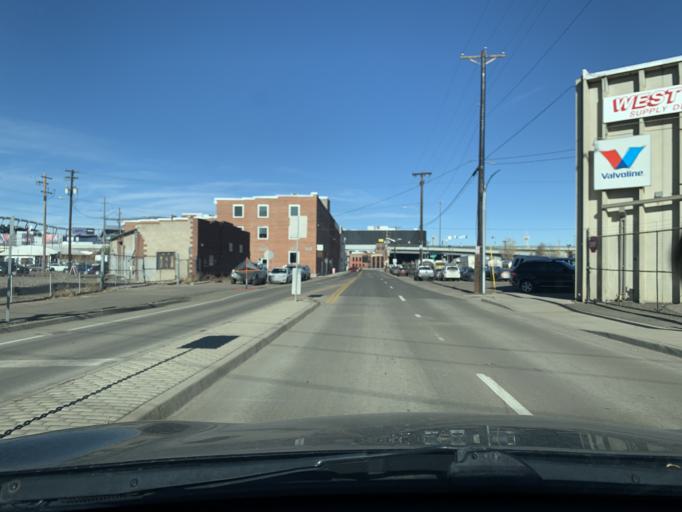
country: US
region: Colorado
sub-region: Denver County
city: Denver
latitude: 39.7378
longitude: -105.0159
